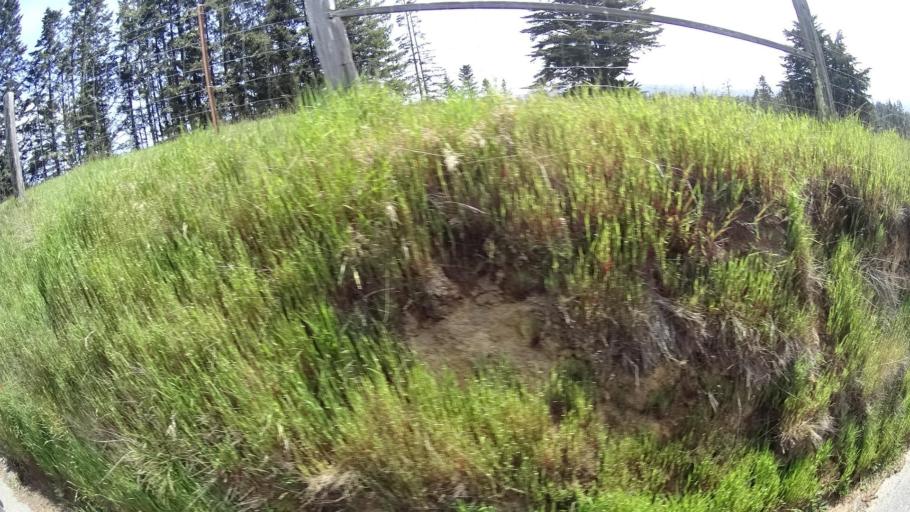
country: US
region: California
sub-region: Humboldt County
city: Fortuna
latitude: 40.6189
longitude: -124.1793
